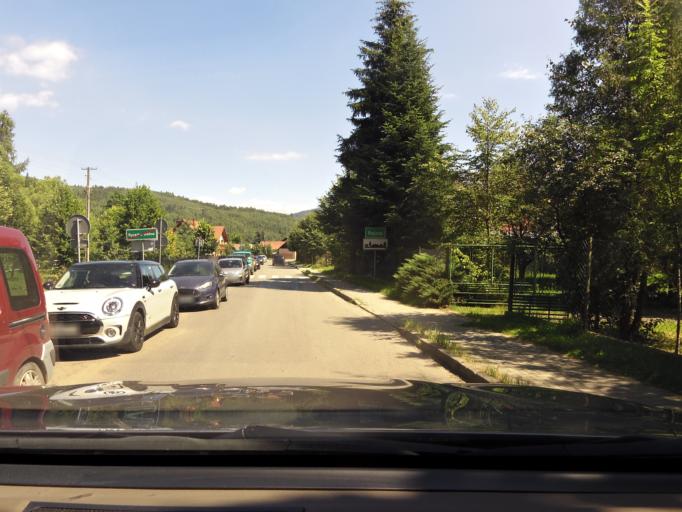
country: PL
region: Silesian Voivodeship
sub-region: Powiat zywiecki
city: Rajcza
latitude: 49.4991
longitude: 19.0921
